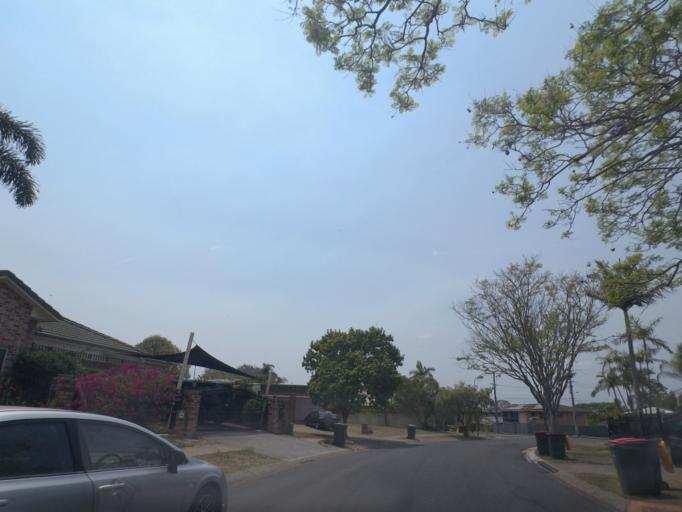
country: AU
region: Queensland
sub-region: Brisbane
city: Nathan
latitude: -27.5613
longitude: 153.0620
